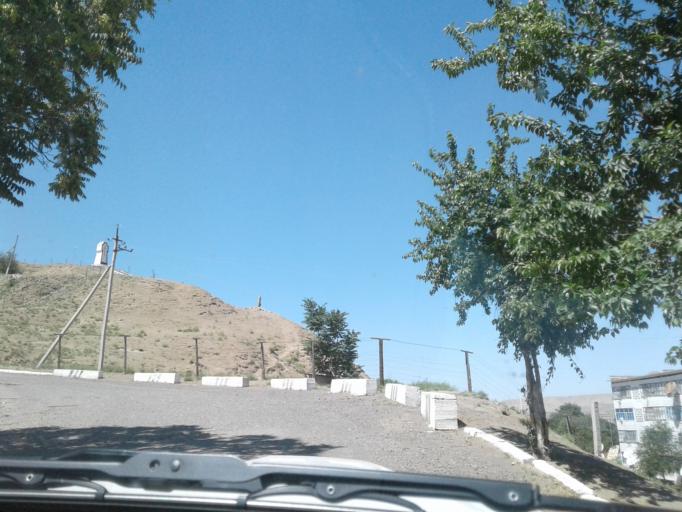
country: TM
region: Mary
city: Serhetabat
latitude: 35.2786
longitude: 62.3436
